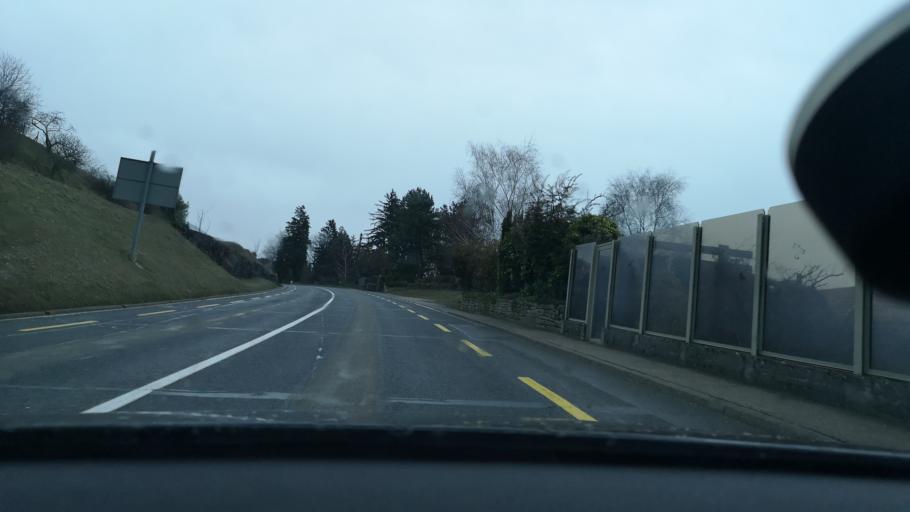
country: CH
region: Neuchatel
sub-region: Boudry District
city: Saint-Aubin-Sauges
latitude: 46.8805
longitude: 6.7614
